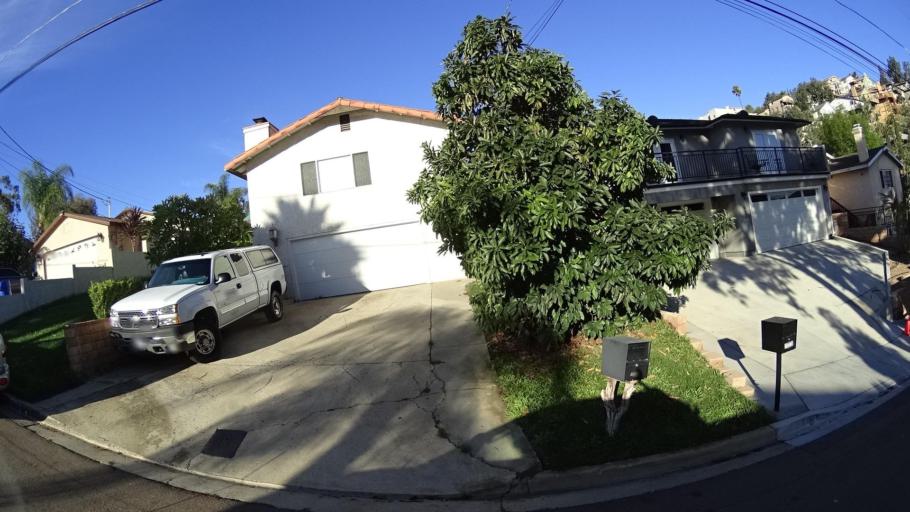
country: US
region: California
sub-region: San Diego County
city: La Presa
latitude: 32.7186
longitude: -116.9853
